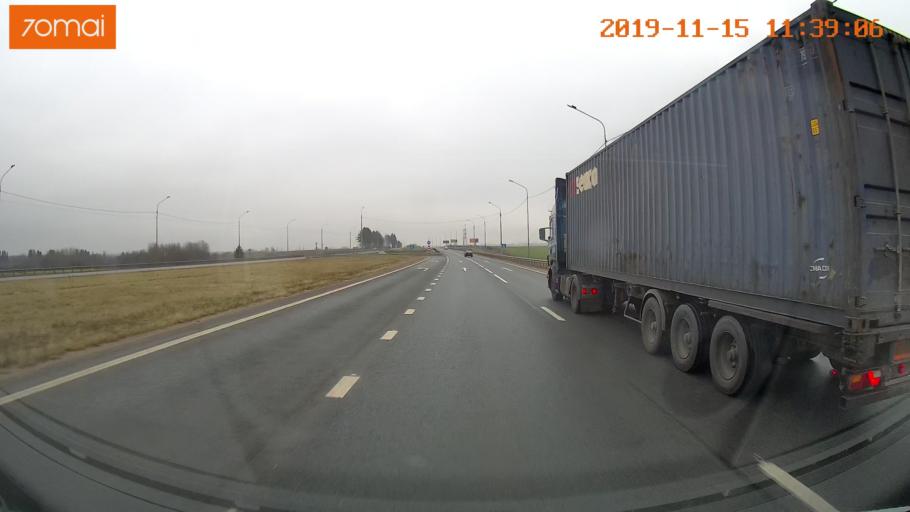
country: RU
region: Vologda
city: Molochnoye
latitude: 59.2110
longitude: 39.7153
